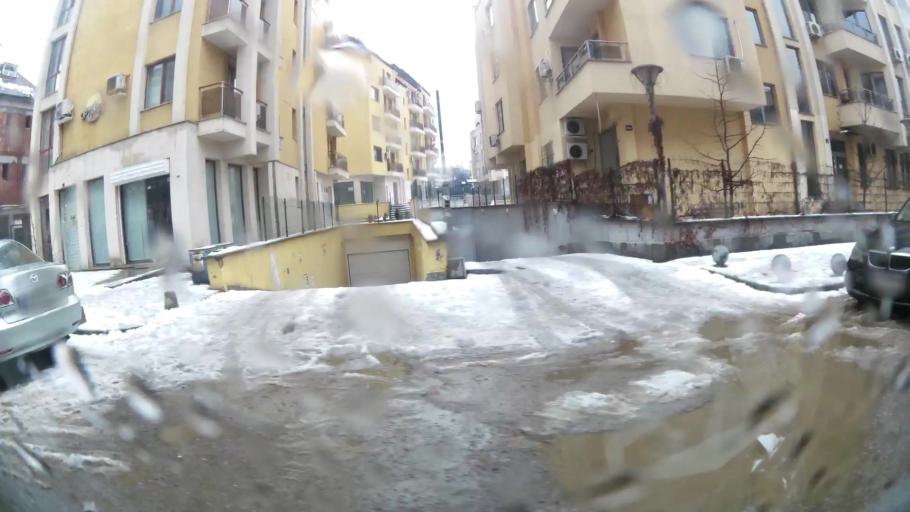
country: BG
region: Sofia-Capital
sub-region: Stolichna Obshtina
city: Sofia
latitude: 42.6618
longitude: 23.2801
